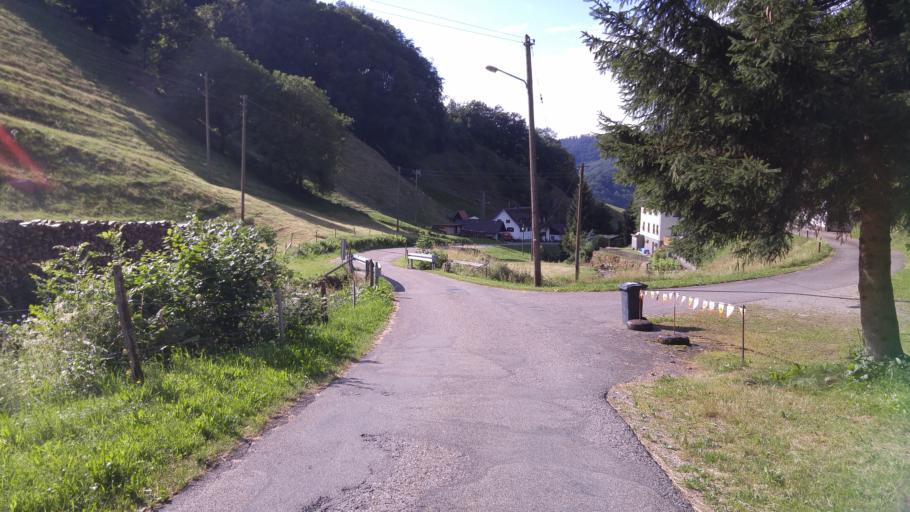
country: DE
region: Baden-Wuerttemberg
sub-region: Freiburg Region
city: Wieden
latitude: 47.8665
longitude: 7.8485
